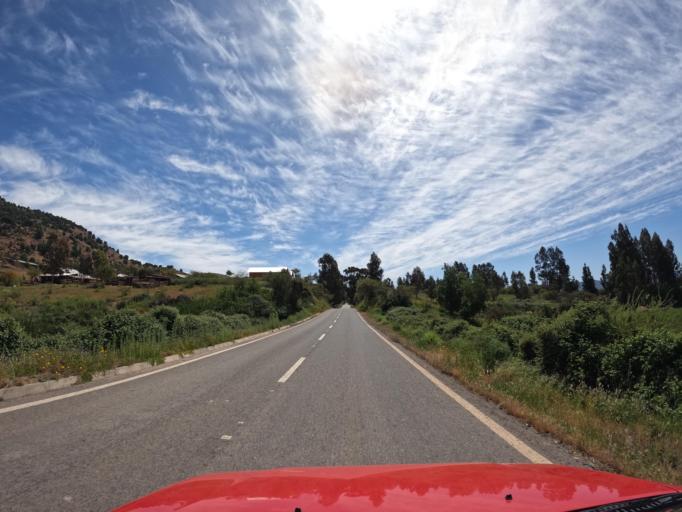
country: CL
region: Maule
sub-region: Provincia de Talca
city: Talca
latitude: -35.0598
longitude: -71.7386
